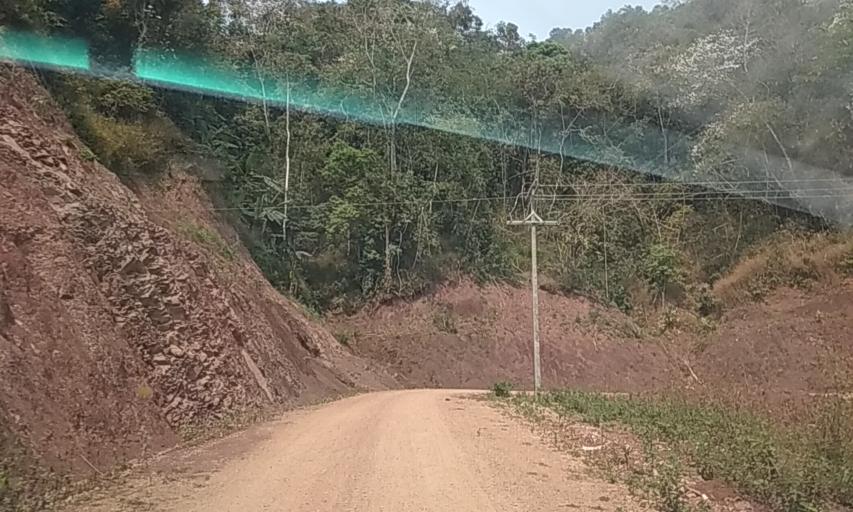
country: VN
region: Huyen Dien Bien
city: Dien Bien Phu
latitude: 21.4547
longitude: 102.7664
